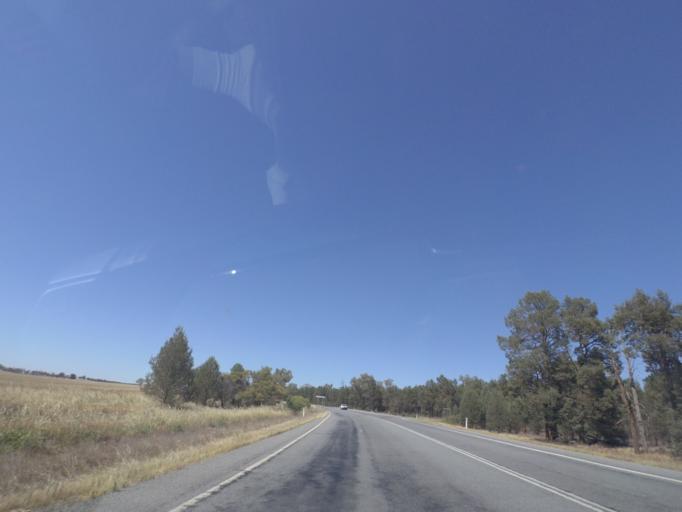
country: AU
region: New South Wales
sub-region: Narrandera
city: Narrandera
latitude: -34.4211
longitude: 146.8456
